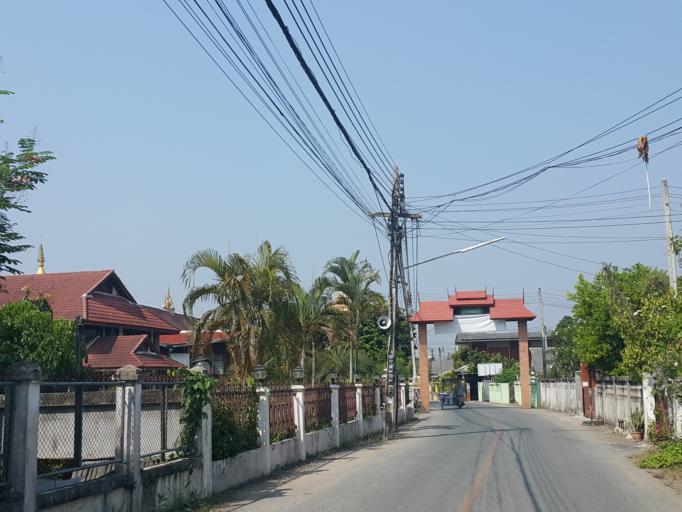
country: TH
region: Chiang Mai
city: San Kamphaeng
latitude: 18.7421
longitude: 99.1293
